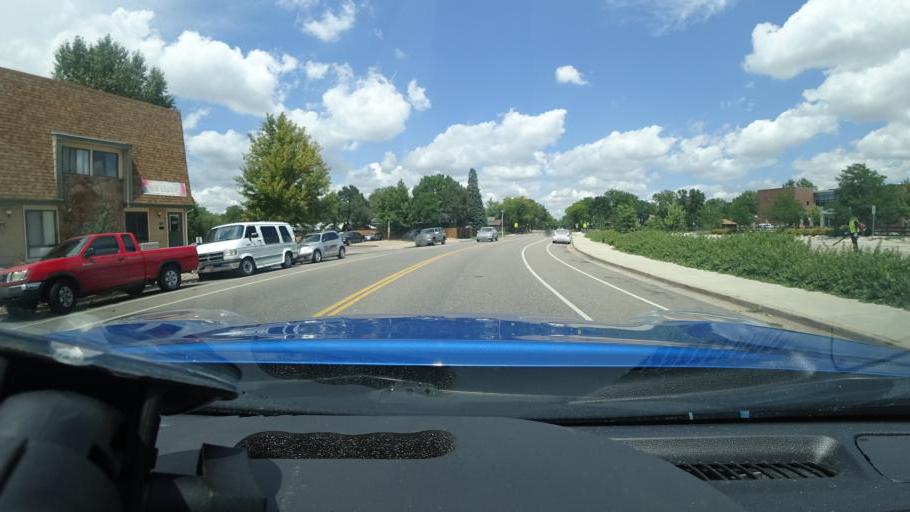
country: US
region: Colorado
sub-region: Adams County
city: Aurora
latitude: 39.6991
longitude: -104.8410
